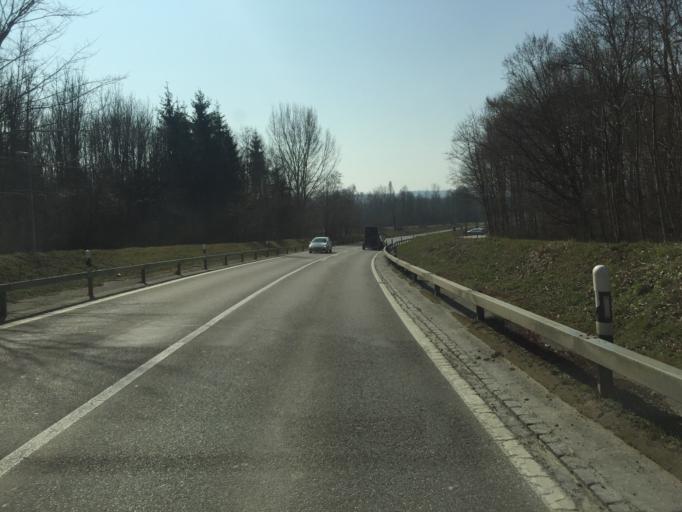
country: CH
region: Thurgau
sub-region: Frauenfeld District
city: Frauenfeld
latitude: 47.5781
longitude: 8.8846
